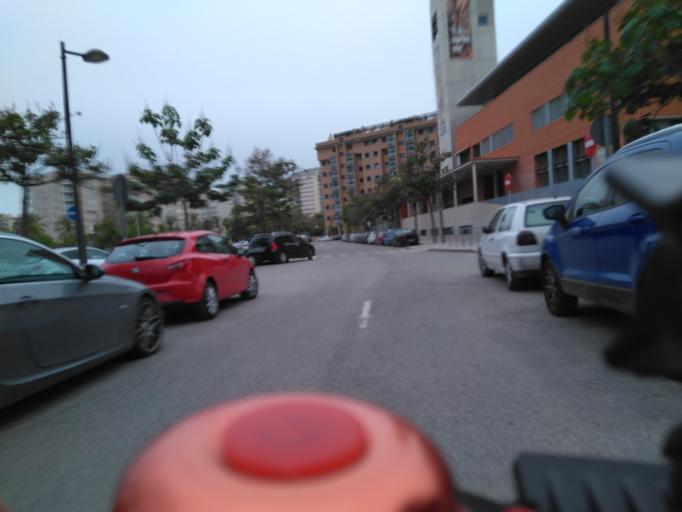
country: ES
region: Valencia
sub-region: Provincia de Valencia
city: Mislata
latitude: 39.4901
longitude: -0.4033
